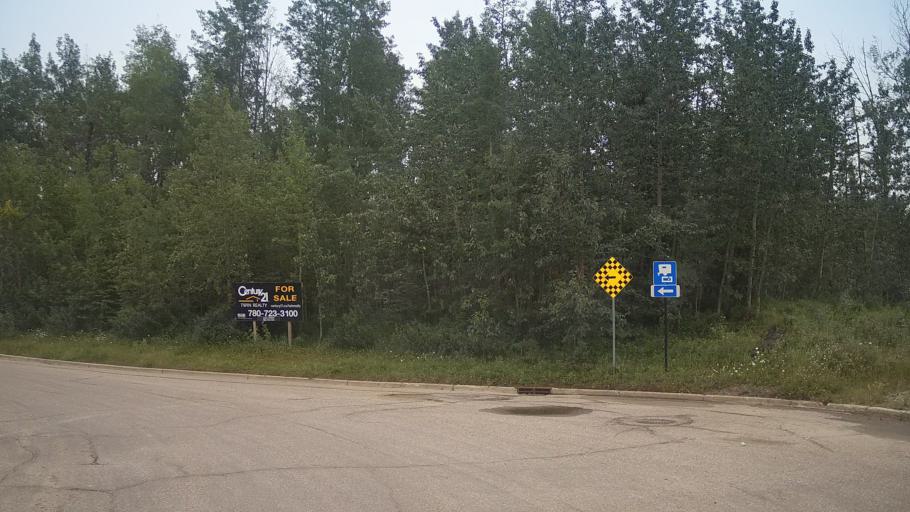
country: CA
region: Alberta
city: Edson
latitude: 53.5761
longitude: -116.4462
